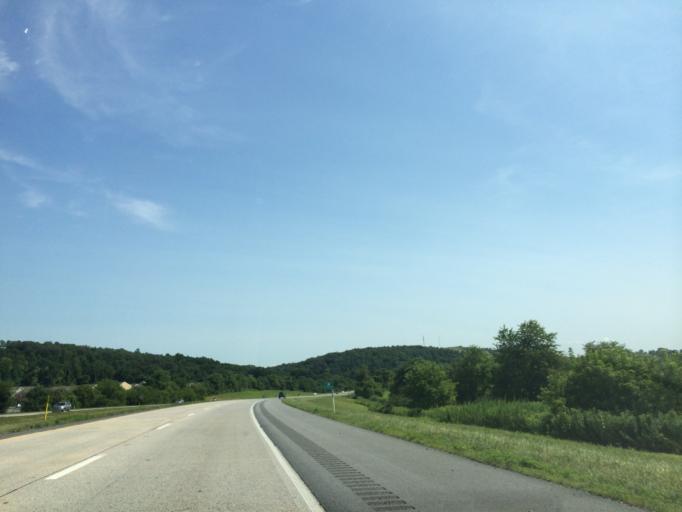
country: US
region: Pennsylvania
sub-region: Berks County
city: Kutztown
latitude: 40.5217
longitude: -75.7889
